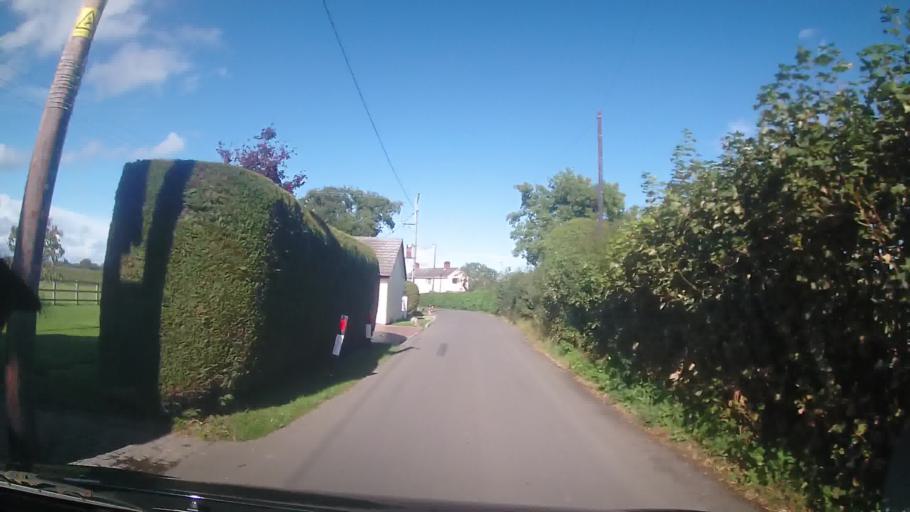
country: GB
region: England
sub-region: Shropshire
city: Wem
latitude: 52.8497
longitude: -2.7029
